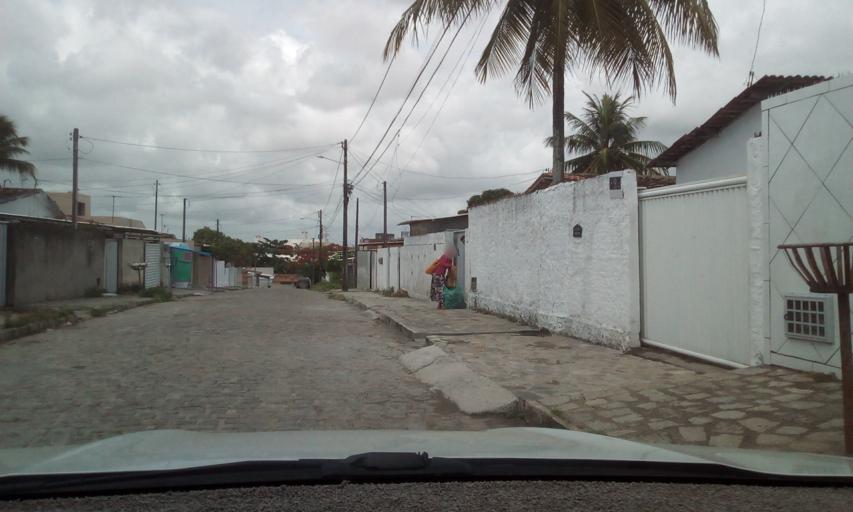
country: BR
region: Paraiba
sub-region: Joao Pessoa
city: Joao Pessoa
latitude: -7.1873
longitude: -34.8402
